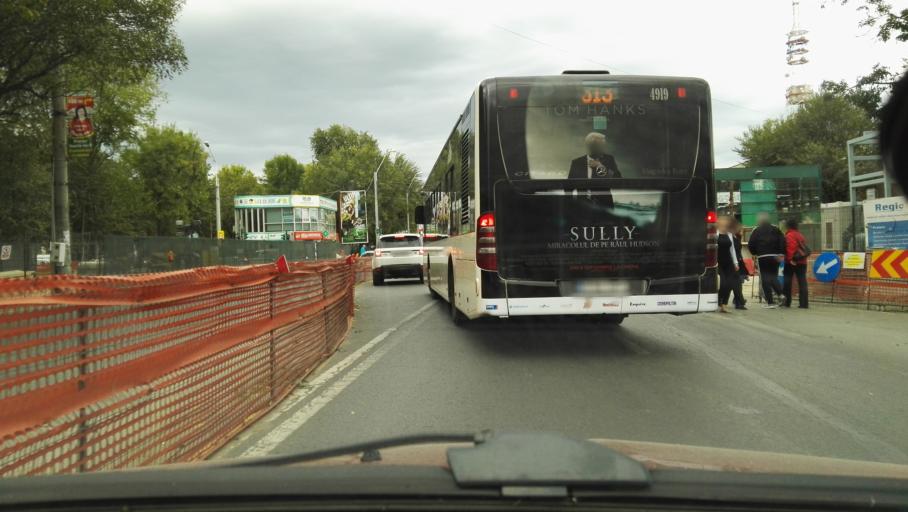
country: RO
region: Bucuresti
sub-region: Municipiul Bucuresti
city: Bucharest
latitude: 44.3910
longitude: 26.1197
